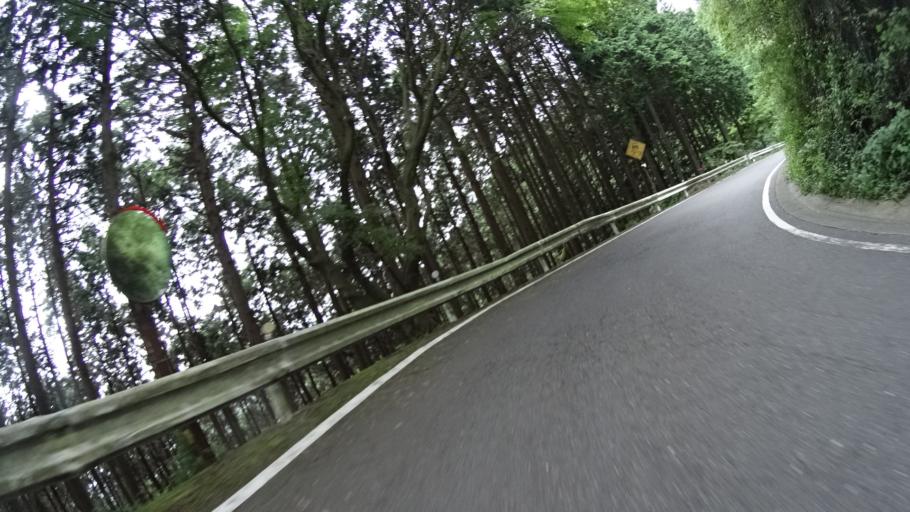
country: JP
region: Kanagawa
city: Hadano
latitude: 35.4248
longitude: 139.2208
